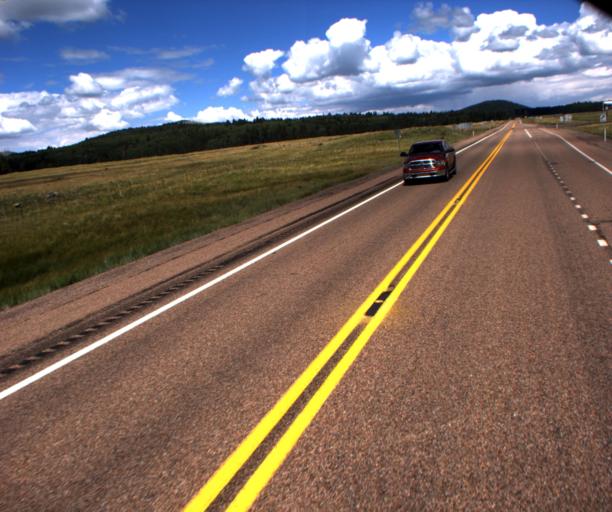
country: US
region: Arizona
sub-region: Apache County
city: Eagar
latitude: 34.0424
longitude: -109.5940
